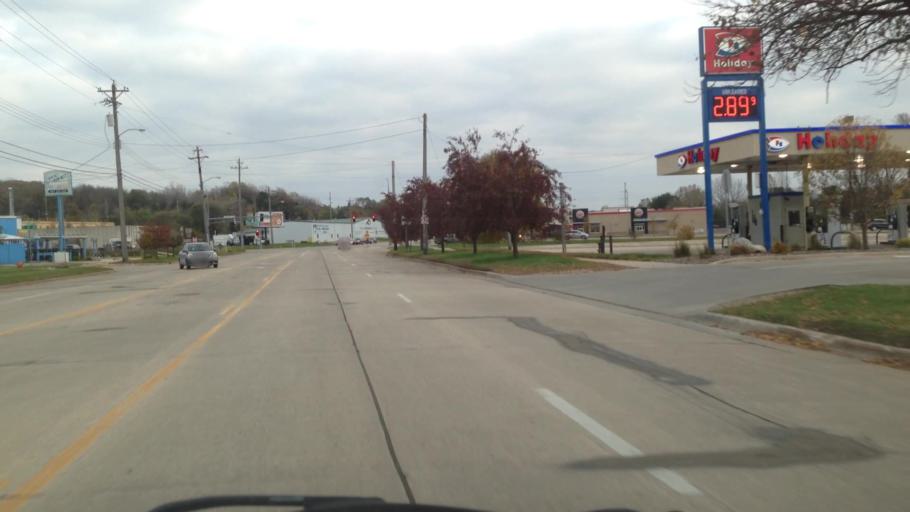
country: US
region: Minnesota
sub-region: Olmsted County
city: Rochester
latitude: 44.0102
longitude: -92.4432
